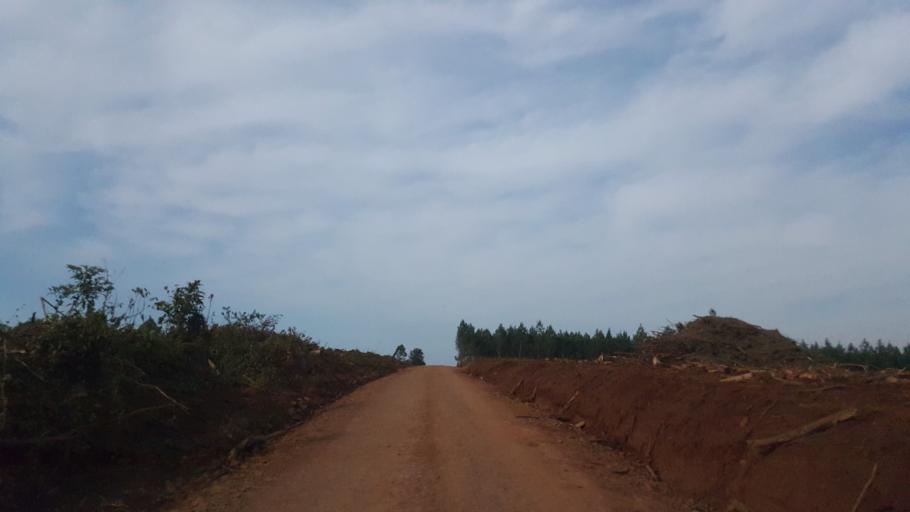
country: AR
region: Misiones
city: Capiovi
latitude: -26.9188
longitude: -55.1164
